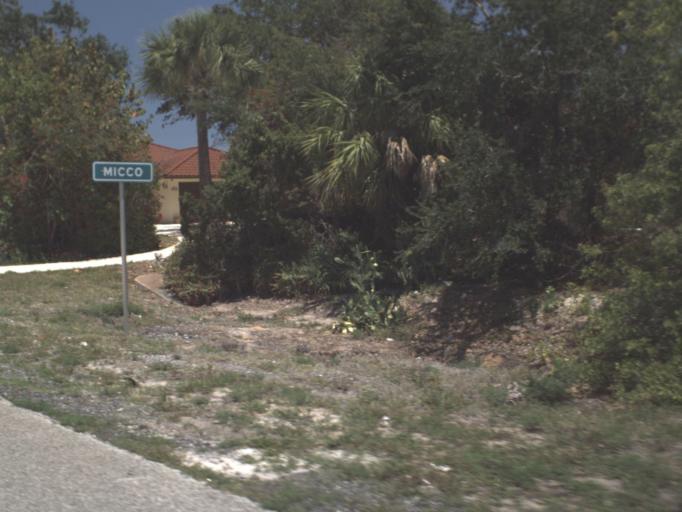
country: US
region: Florida
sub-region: Indian River County
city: Roseland
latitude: 27.8569
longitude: -80.4917
